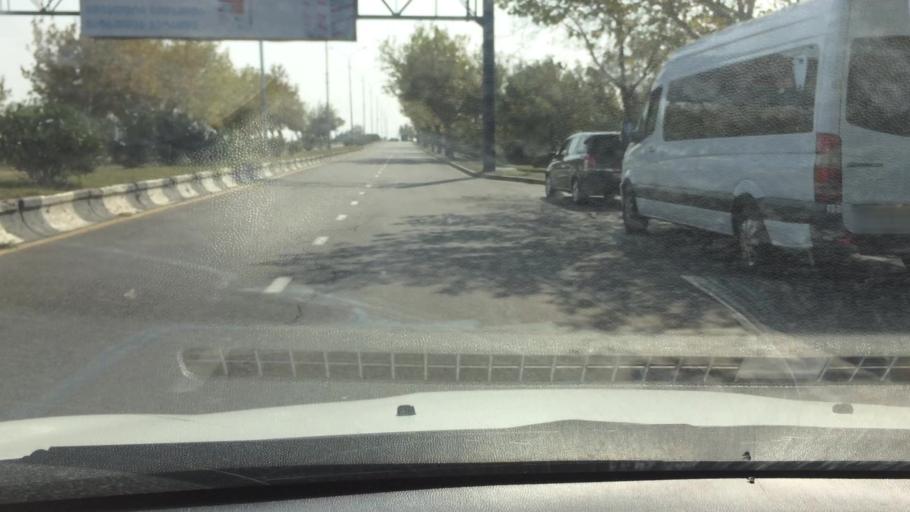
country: GE
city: Didi Lilo
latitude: 41.6891
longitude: 44.9529
